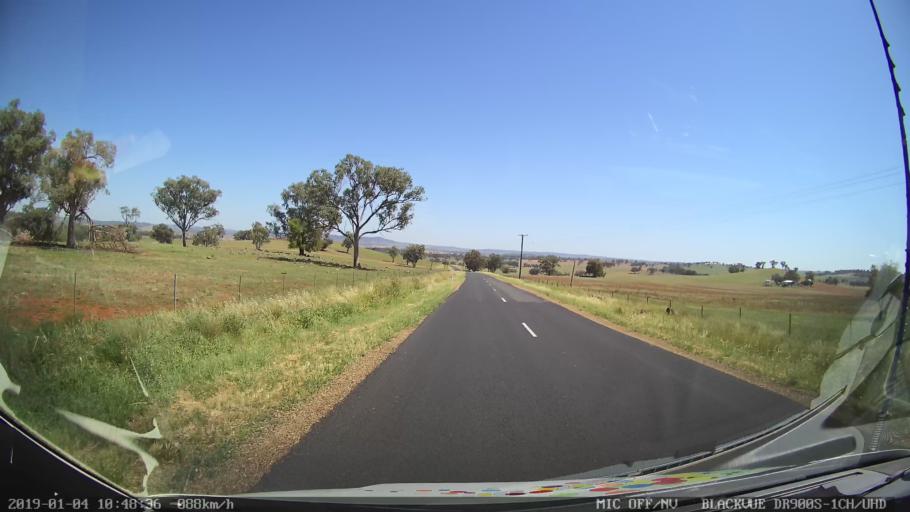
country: AU
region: New South Wales
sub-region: Cabonne
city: Molong
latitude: -33.2578
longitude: 148.7123
